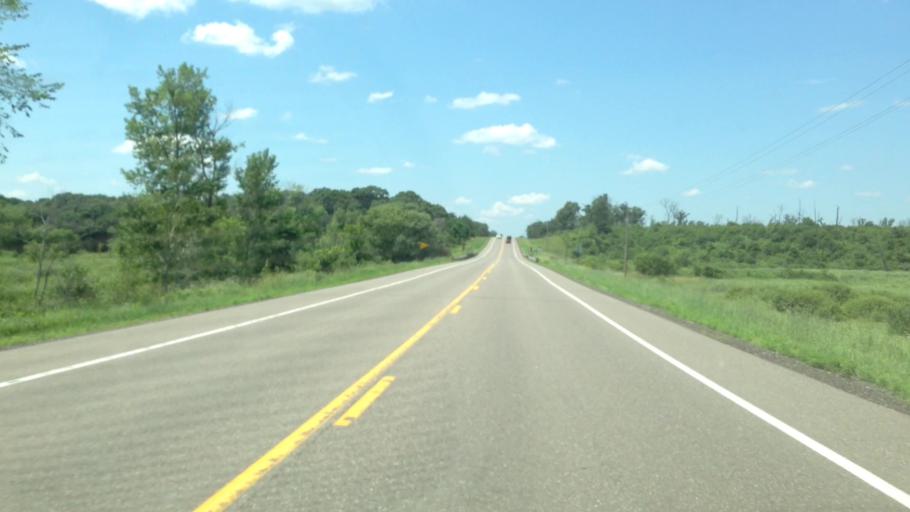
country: US
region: Minnesota
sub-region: Sherburne County
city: Zimmerman
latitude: 45.4438
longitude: -93.6525
